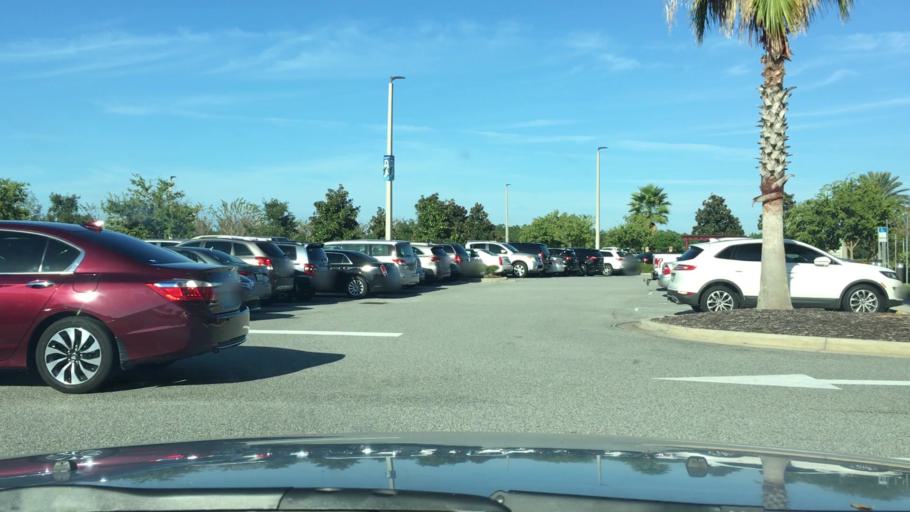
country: US
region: Florida
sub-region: Volusia County
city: Ormond Beach
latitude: 29.2421
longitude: -81.1083
